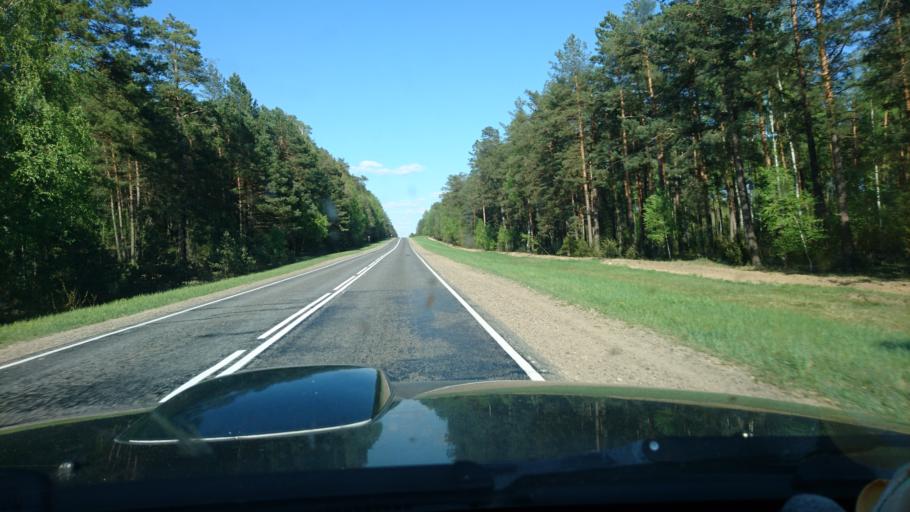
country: BY
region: Brest
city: Kobryn
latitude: 52.4087
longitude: 24.1931
